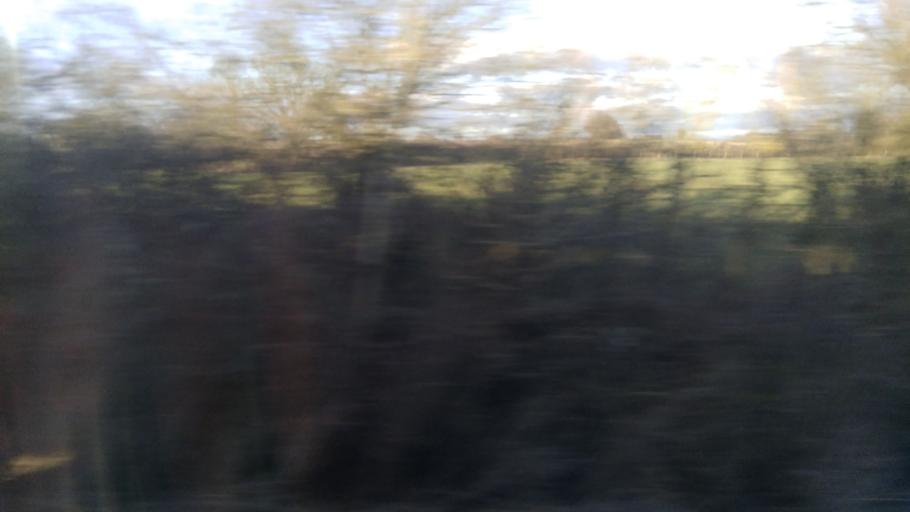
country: GB
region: England
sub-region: Kent
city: Staplehurst
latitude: 51.1733
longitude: 0.5251
